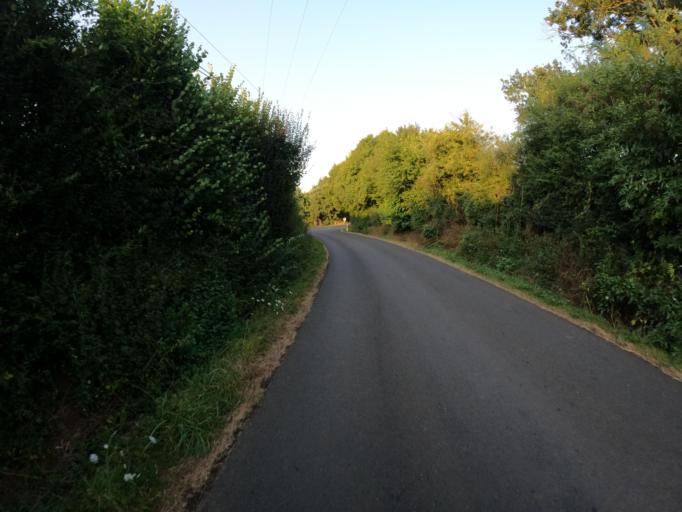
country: FR
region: Pays de la Loire
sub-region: Departement de la Sarthe
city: Brulon
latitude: 47.9307
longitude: -0.2283
